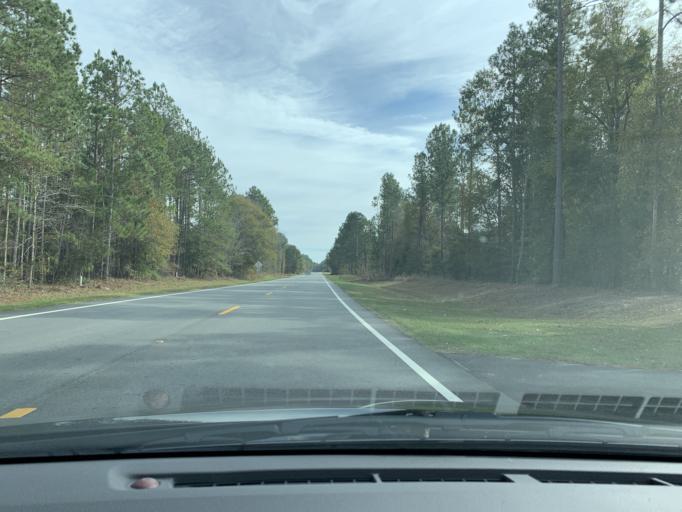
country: US
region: Georgia
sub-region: Wilcox County
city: Rochelle
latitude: 31.9587
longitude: -83.5853
